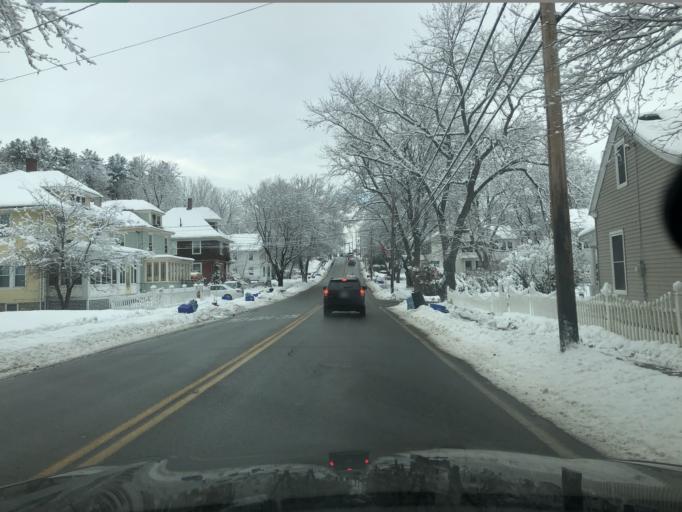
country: US
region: New Hampshire
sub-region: Strafford County
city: Somersworth
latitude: 43.2566
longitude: -70.8684
